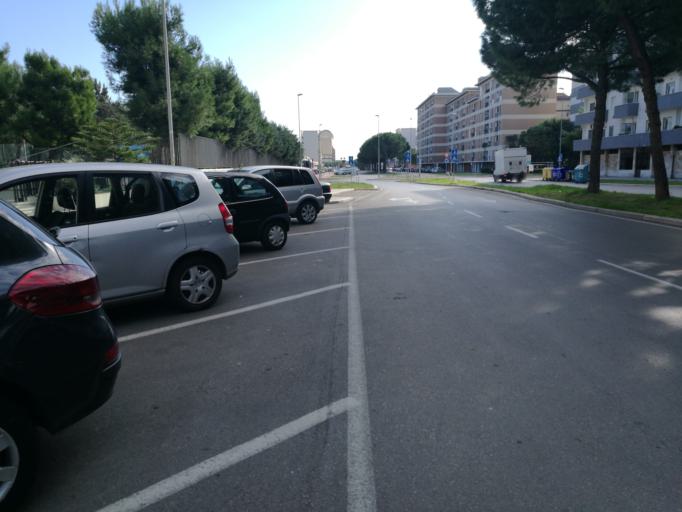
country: IT
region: Apulia
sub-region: Provincia di Bari
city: Bari
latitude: 41.1091
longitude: 16.8929
